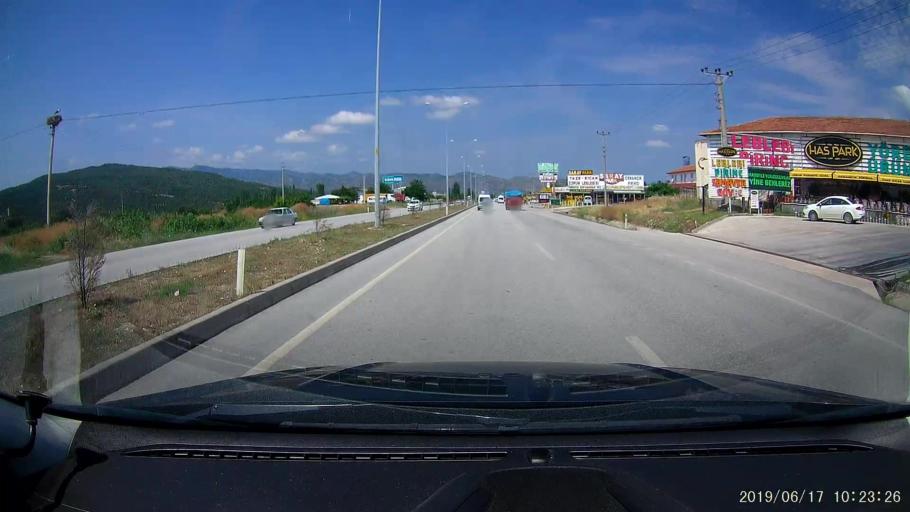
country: TR
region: Corum
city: Osmancik
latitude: 40.9708
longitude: 34.8381
